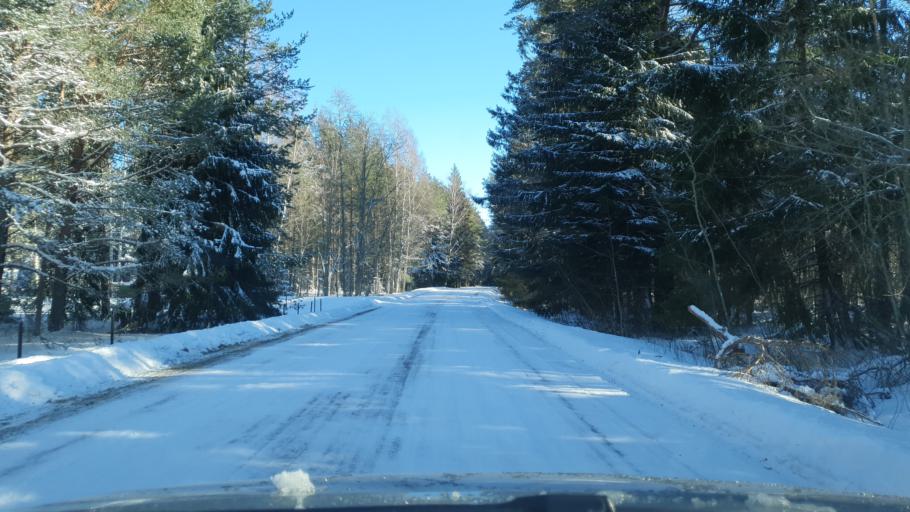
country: EE
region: Harju
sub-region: Loksa linn
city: Loksa
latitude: 59.6157
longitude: 26.0144
